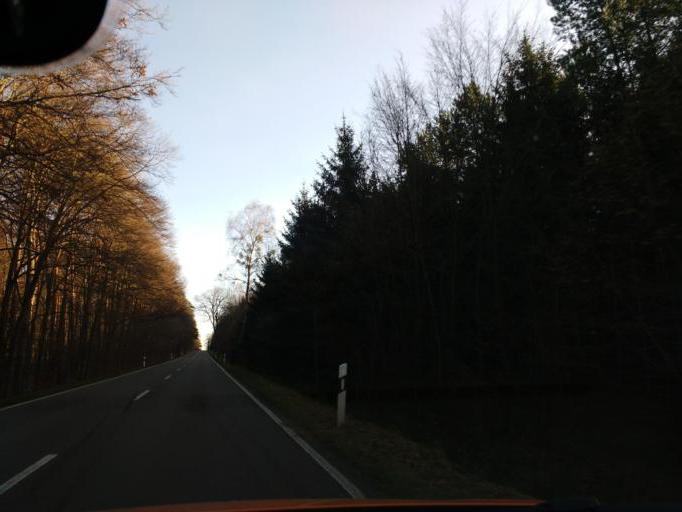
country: DE
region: Brandenburg
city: Protzel
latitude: 52.6448
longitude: 13.9430
